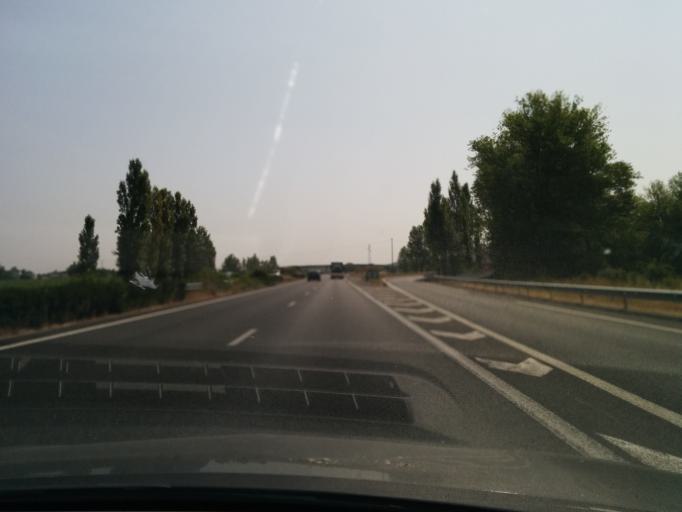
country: FR
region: Midi-Pyrenees
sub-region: Departement du Tarn
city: Lagrave
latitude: 43.8890
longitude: 1.9627
